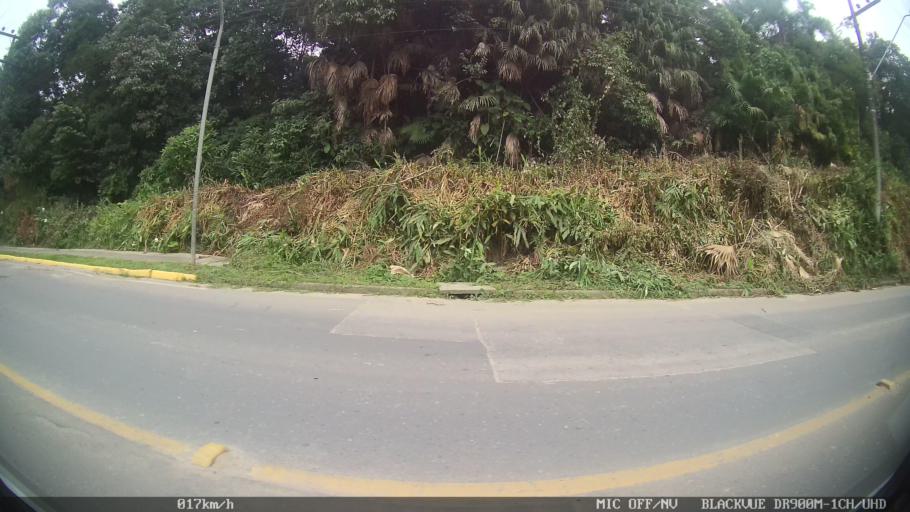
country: BR
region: Santa Catarina
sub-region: Joinville
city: Joinville
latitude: -26.3772
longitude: -48.8435
